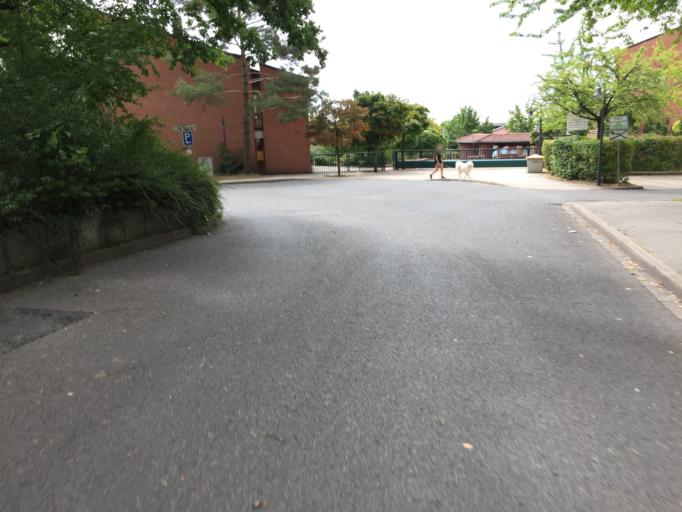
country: DE
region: Bavaria
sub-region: Regierungsbezirk Mittelfranken
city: Erlangen
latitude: 49.5615
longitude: 11.0020
